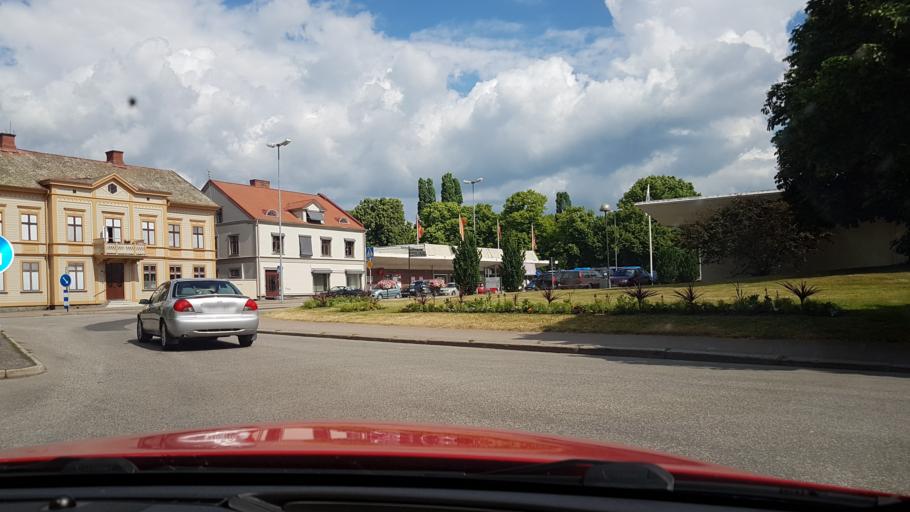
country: SE
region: Vaestra Goetaland
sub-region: Hjo Kommun
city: Hjo
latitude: 58.3035
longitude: 14.2915
